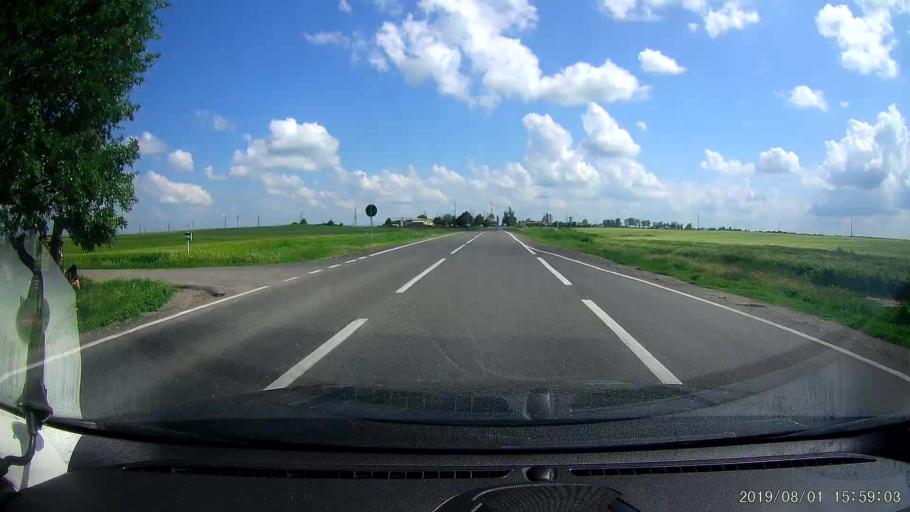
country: RO
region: Ialomita
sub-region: Comuna Slobozia
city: Slobozia
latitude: 44.5565
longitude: 27.3812
